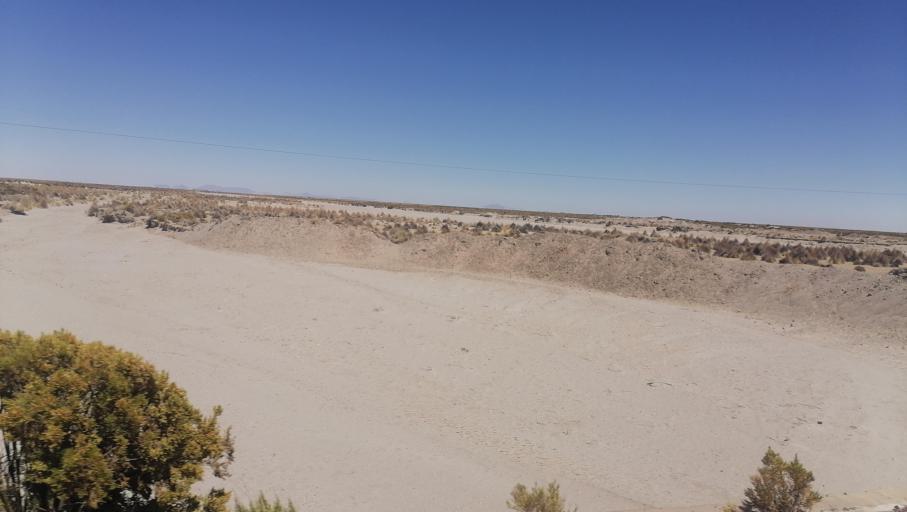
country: BO
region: Oruro
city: Challapata
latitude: -19.1671
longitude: -66.7791
